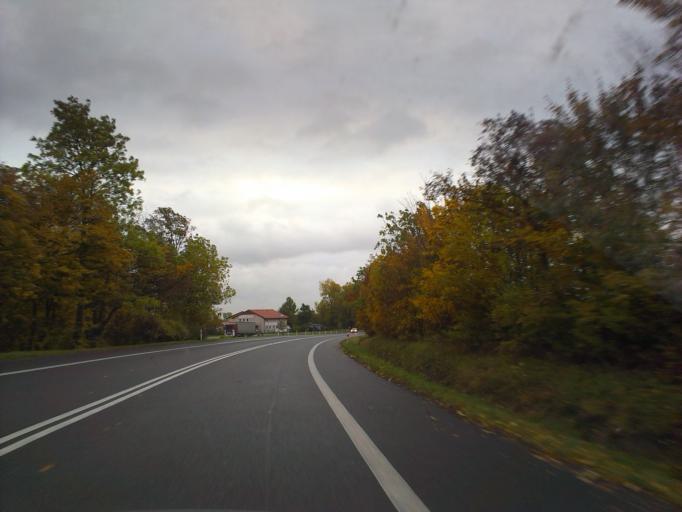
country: PL
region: Kujawsko-Pomorskie
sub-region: Powiat chelminski
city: Chelmno
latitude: 53.3052
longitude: 18.5135
